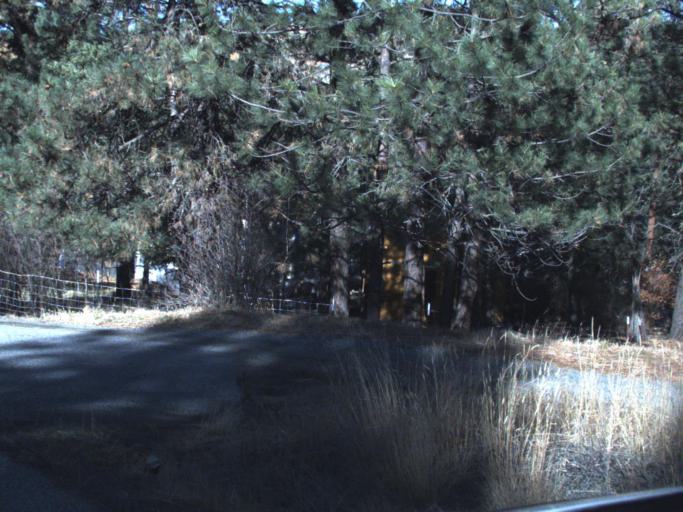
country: US
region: Washington
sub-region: Ferry County
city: Republic
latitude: 48.6513
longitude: -118.6815
